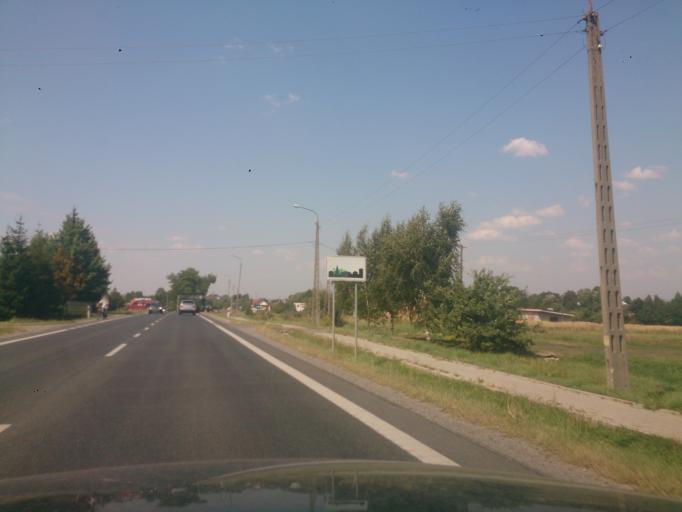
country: PL
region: Subcarpathian Voivodeship
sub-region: Powiat kolbuszowski
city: Kolbuszowa
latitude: 50.2136
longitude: 21.8166
